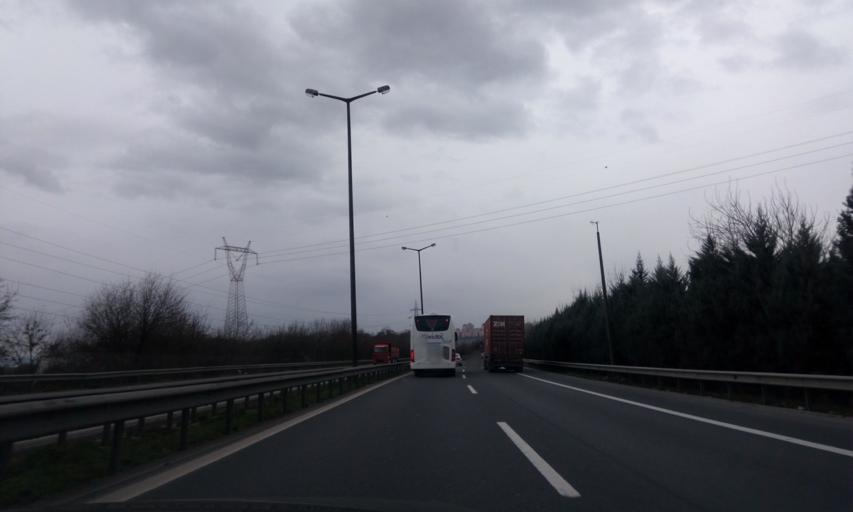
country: TR
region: Kocaeli
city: Kosekoy
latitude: 40.7700
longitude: 29.9899
